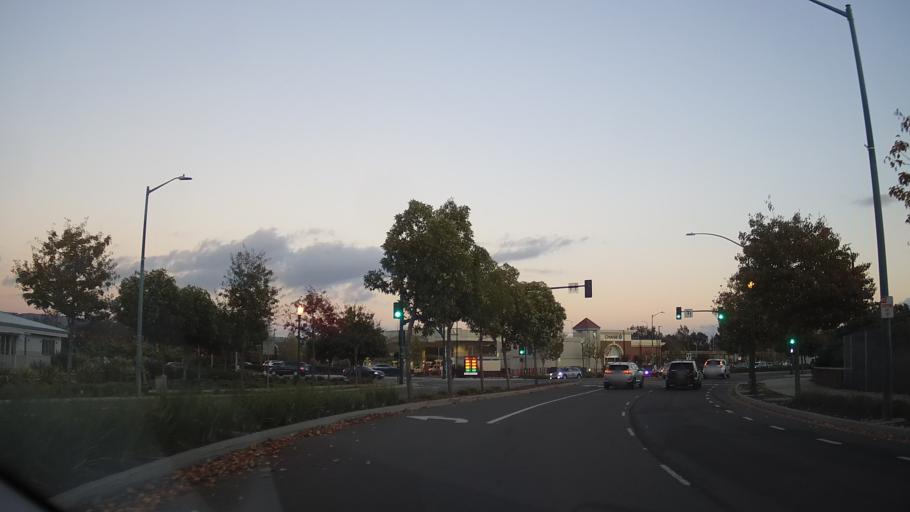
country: US
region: California
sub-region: Alameda County
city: Oakland
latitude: 37.7850
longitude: -122.2793
